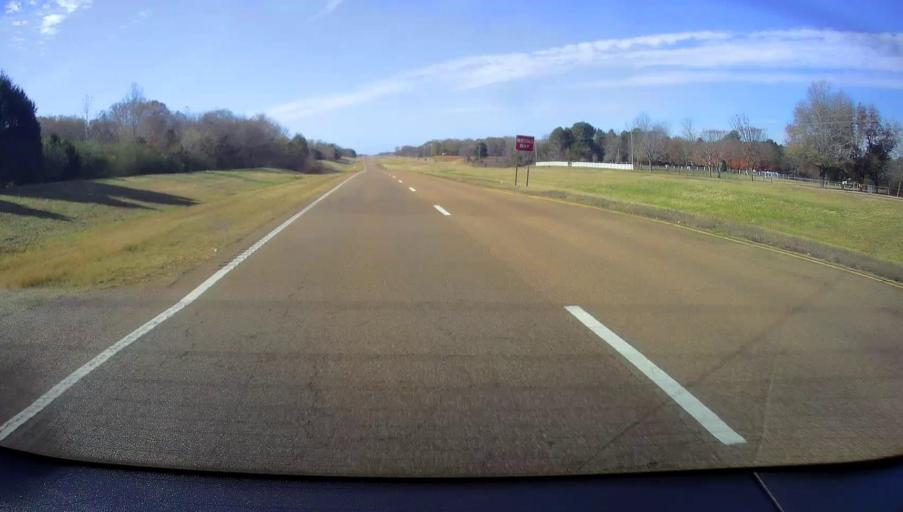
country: US
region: Mississippi
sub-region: Marshall County
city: Holly Springs
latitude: 34.9461
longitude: -89.3537
